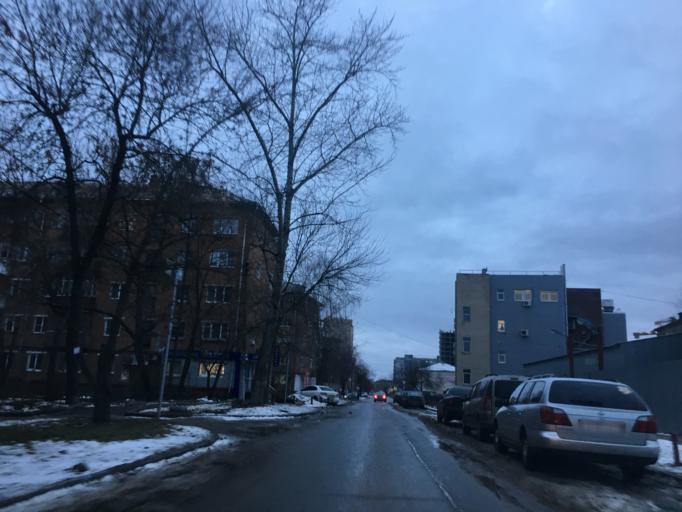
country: RU
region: Tula
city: Tula
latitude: 54.1993
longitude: 37.5930
